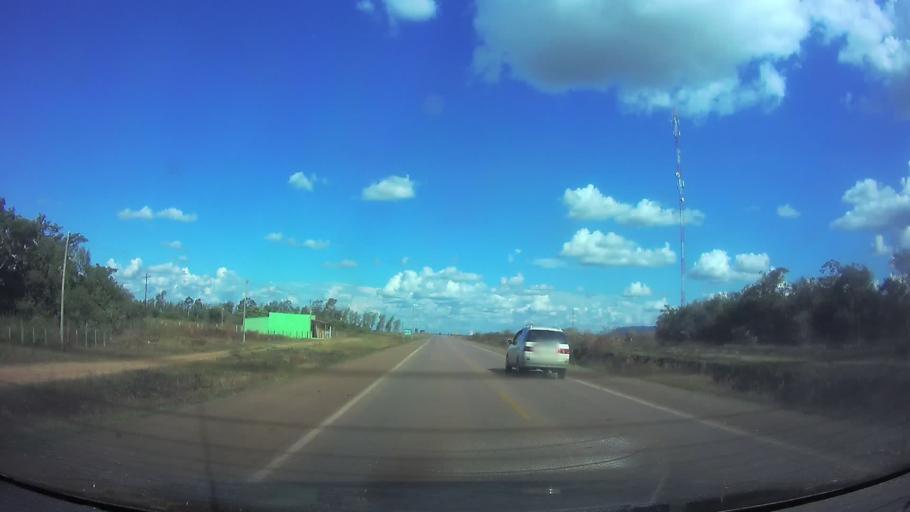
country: PY
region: Paraguari
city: Sapucai
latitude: -25.6962
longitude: -56.8565
